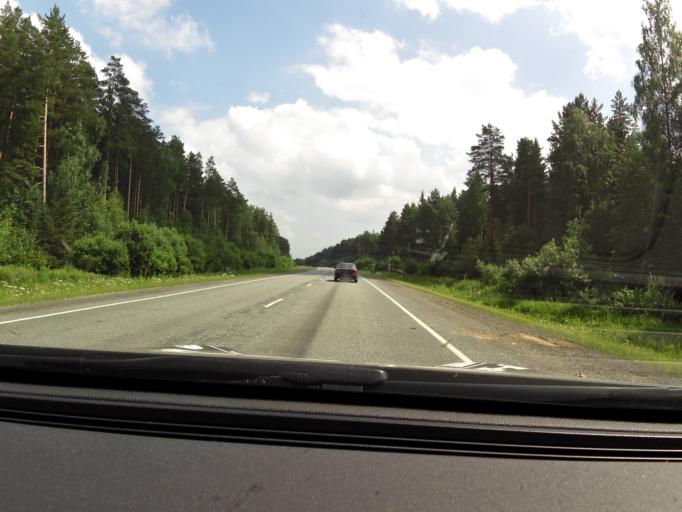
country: RU
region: Sverdlovsk
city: Achit
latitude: 56.8022
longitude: 57.8453
